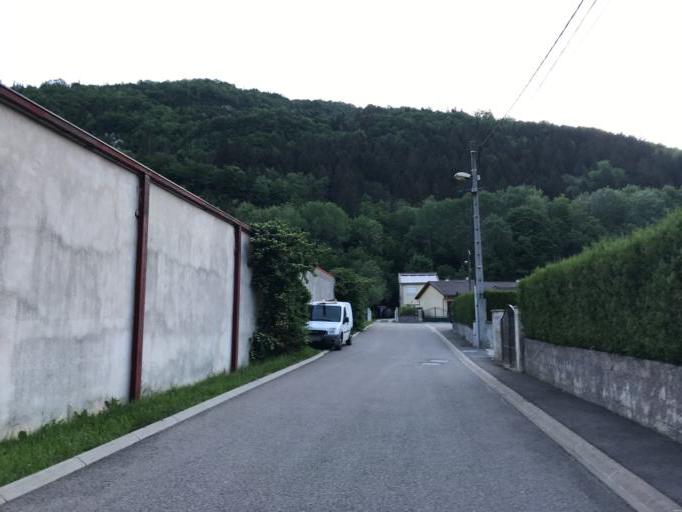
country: FR
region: Rhone-Alpes
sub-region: Departement de l'Ain
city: Oyonnax
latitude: 46.2404
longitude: 5.6680
